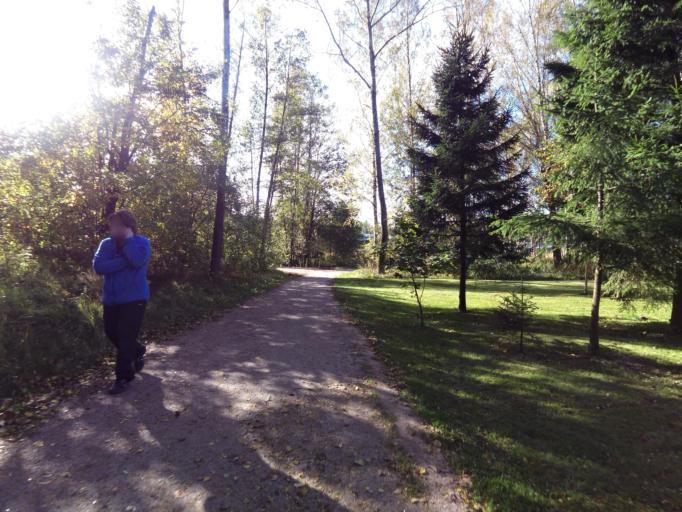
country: FI
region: Uusimaa
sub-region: Helsinki
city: Espoo
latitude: 60.1586
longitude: 24.6131
